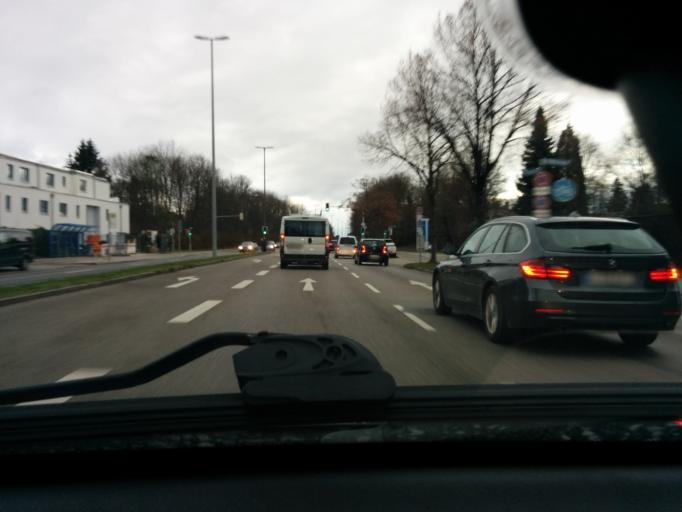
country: DE
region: Bavaria
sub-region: Upper Bavaria
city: Karlsfeld
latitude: 48.1782
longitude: 11.4820
